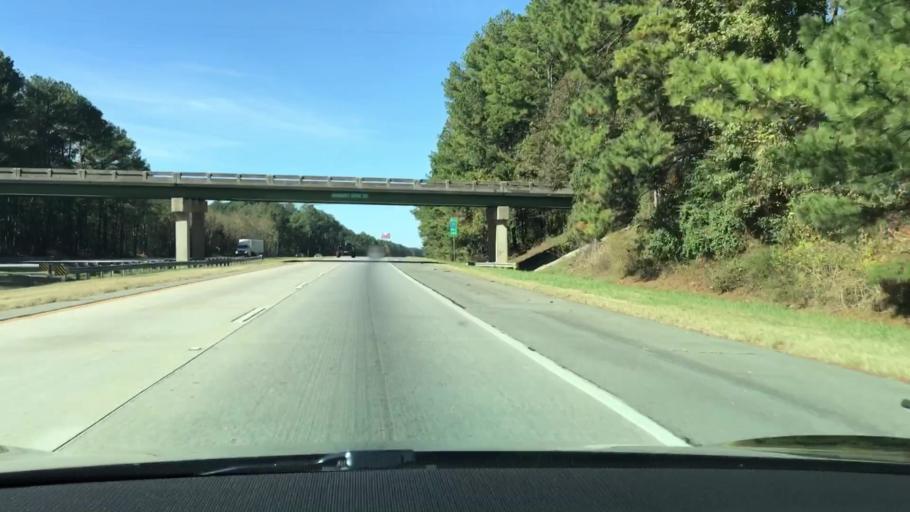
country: US
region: Georgia
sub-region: Taliaferro County
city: Crawfordville
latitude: 33.5280
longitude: -82.9564
